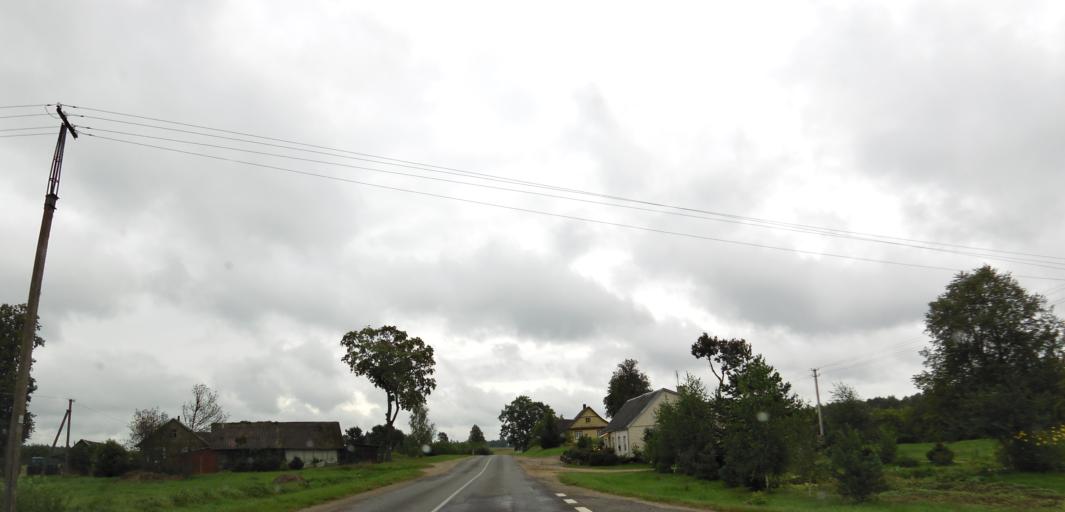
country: LT
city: Moletai
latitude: 55.2917
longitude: 25.3456
